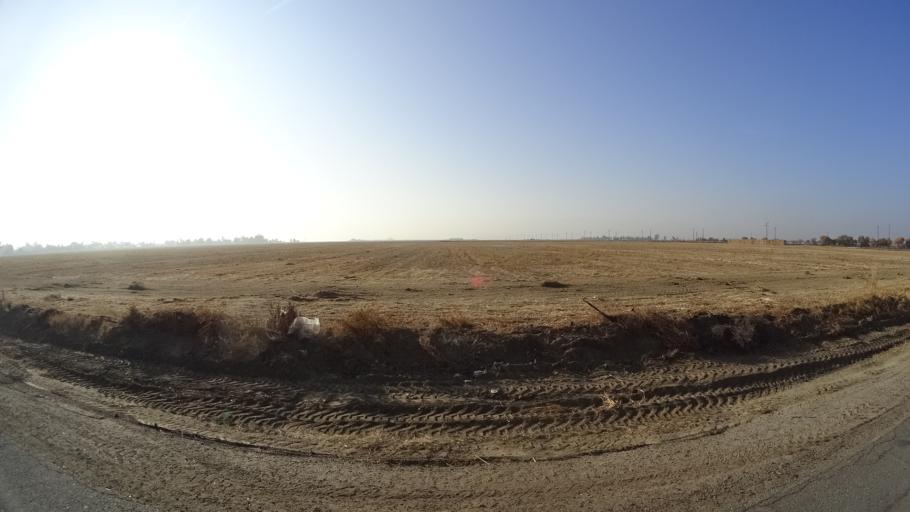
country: US
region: California
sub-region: Kern County
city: Greenfield
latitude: 35.2525
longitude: -118.9733
